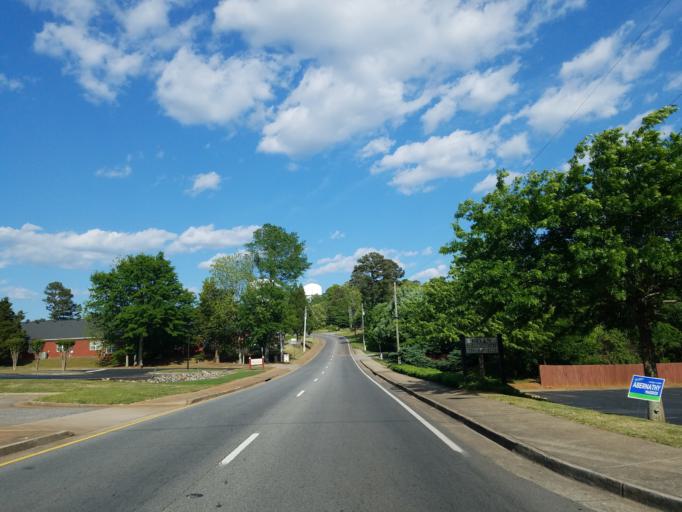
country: US
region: Georgia
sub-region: Forsyth County
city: Cumming
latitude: 34.2056
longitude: -84.1351
